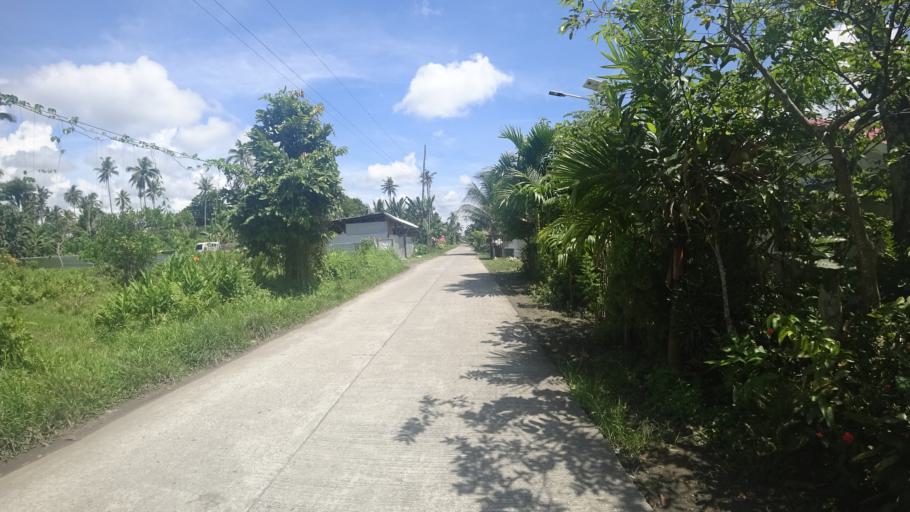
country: PH
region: Eastern Visayas
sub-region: Province of Leyte
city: Alangalang
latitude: 11.2306
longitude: 124.8438
